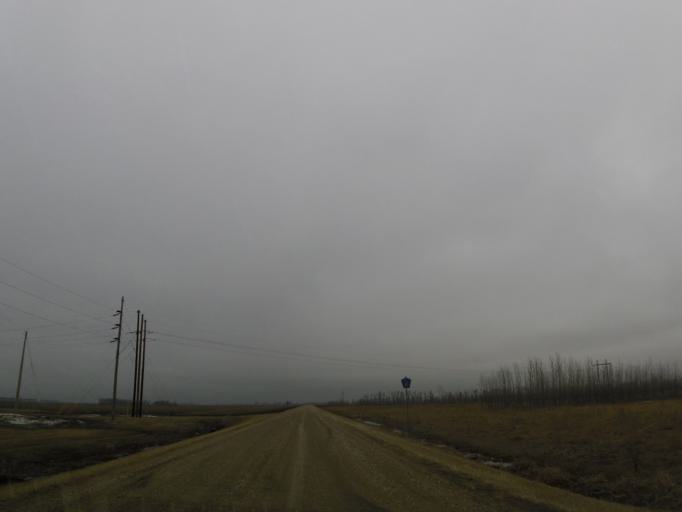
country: US
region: North Dakota
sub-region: Walsh County
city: Grafton
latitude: 48.3535
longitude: -97.1674
